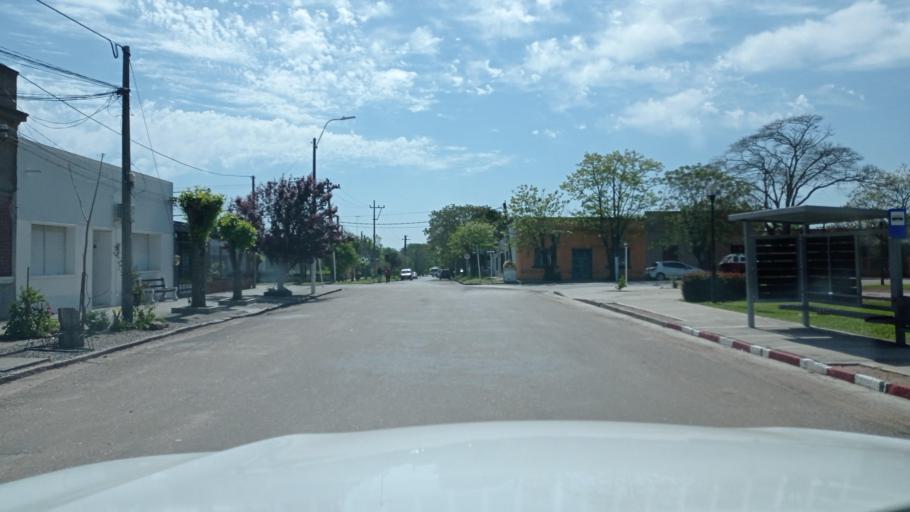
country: UY
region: Canelones
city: Santa Rosa
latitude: -34.4979
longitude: -56.0412
